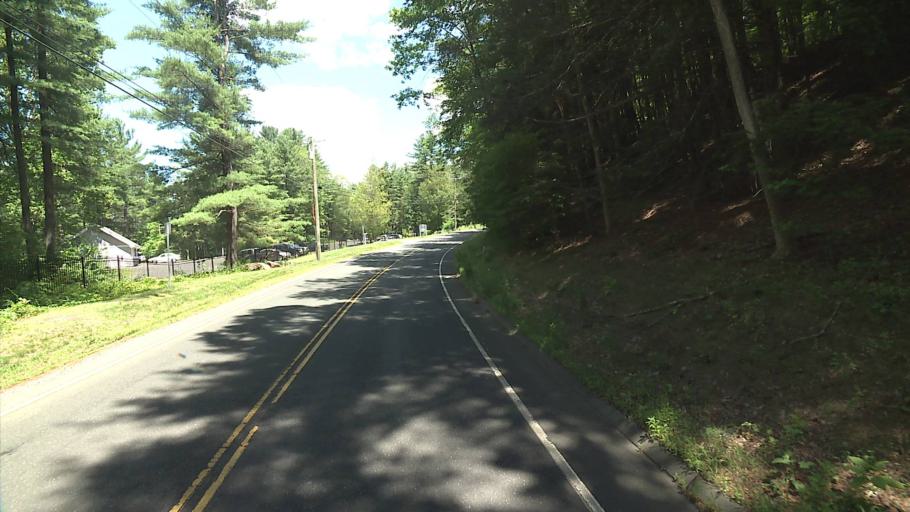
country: US
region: Connecticut
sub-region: Litchfield County
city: New Hartford Center
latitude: 41.9040
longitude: -72.9567
